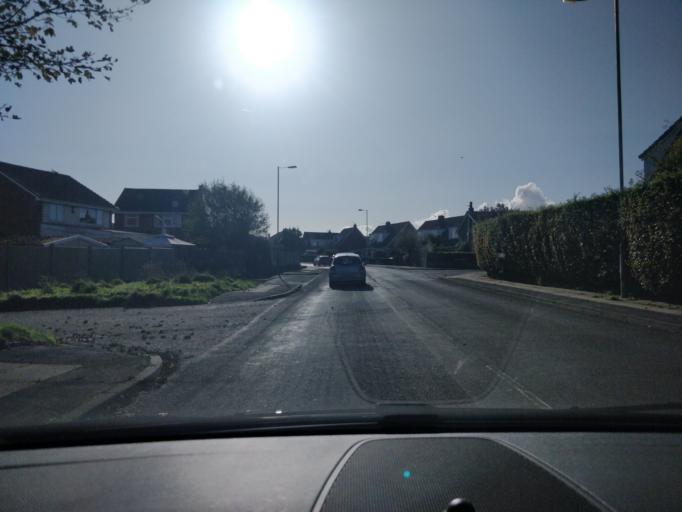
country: GB
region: England
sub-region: Lancashire
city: Banks
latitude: 53.6781
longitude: -2.9456
